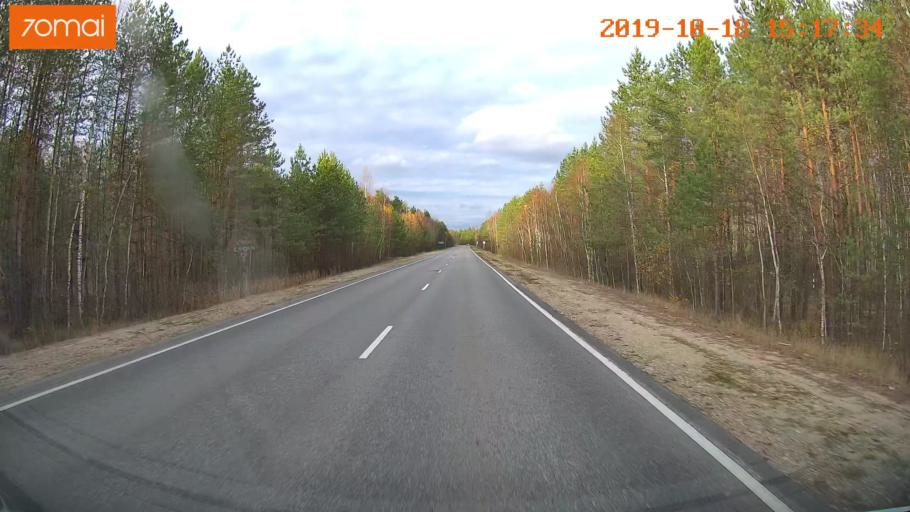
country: RU
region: Vladimir
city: Anopino
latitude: 55.6518
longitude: 40.7268
